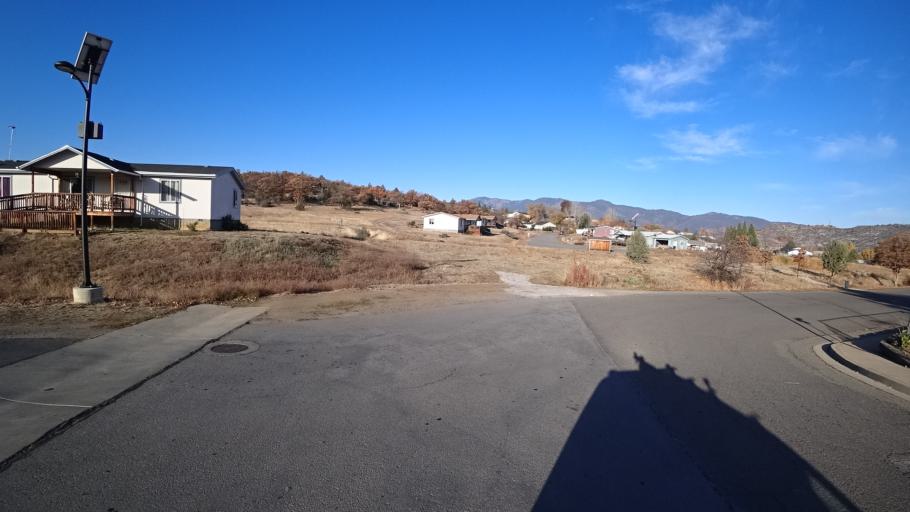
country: US
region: California
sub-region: Siskiyou County
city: Yreka
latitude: 41.7070
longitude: -122.6188
